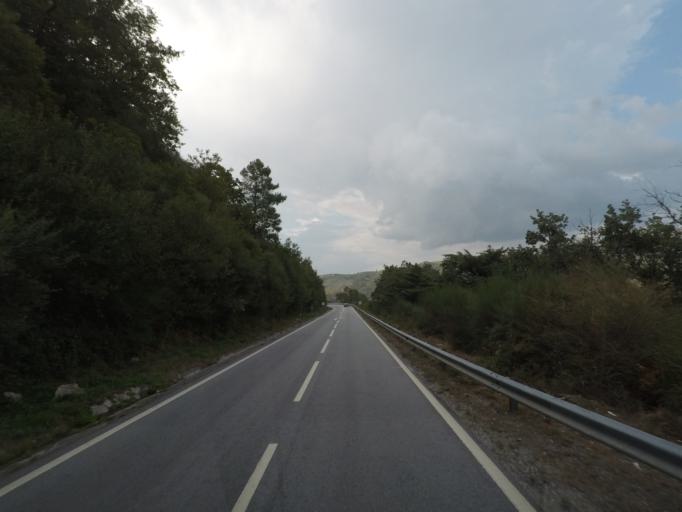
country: PT
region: Porto
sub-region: Baiao
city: Valadares
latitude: 41.2030
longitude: -7.9701
